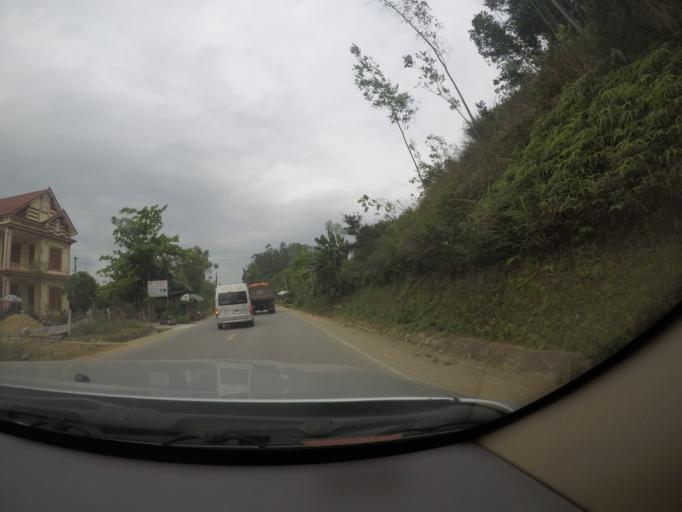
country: VN
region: Quang Binh
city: Ba Don
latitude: 17.6112
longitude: 106.3508
